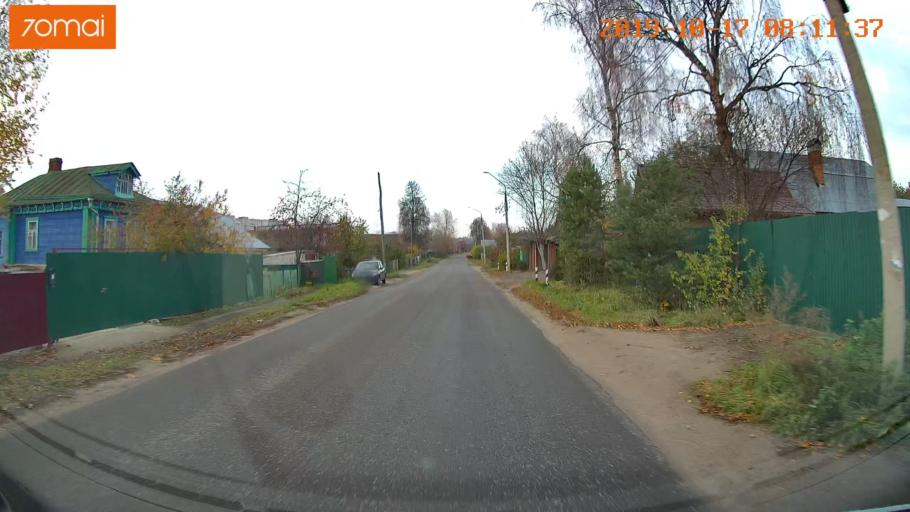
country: RU
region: Vladimir
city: Kol'chugino
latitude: 56.3022
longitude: 39.3671
